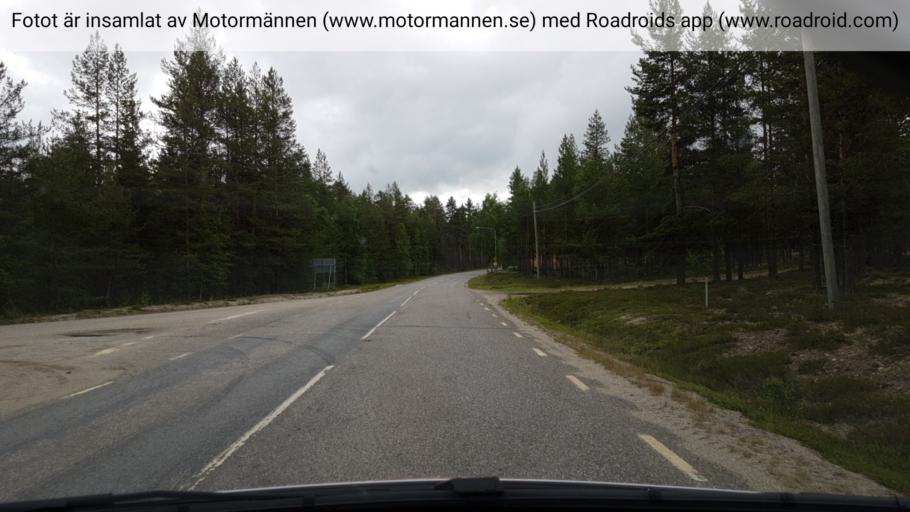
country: SE
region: Vaesterbotten
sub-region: Norsjo Kommun
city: Norsjoe
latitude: 64.6634
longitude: 19.2694
